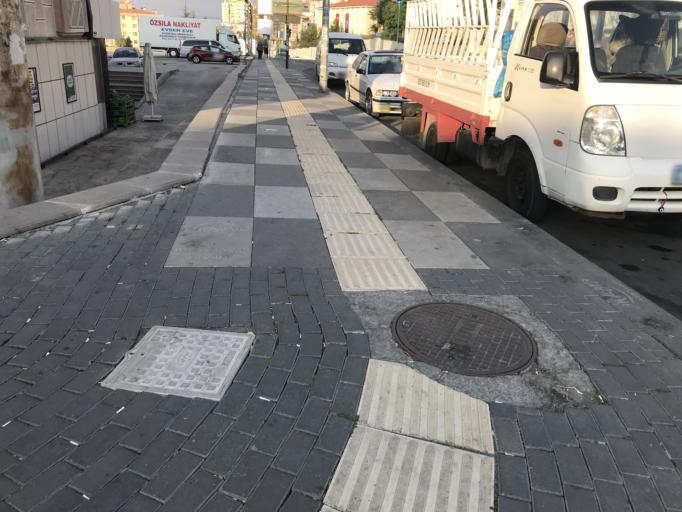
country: TR
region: Ankara
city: Ankara
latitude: 39.8715
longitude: 32.8301
